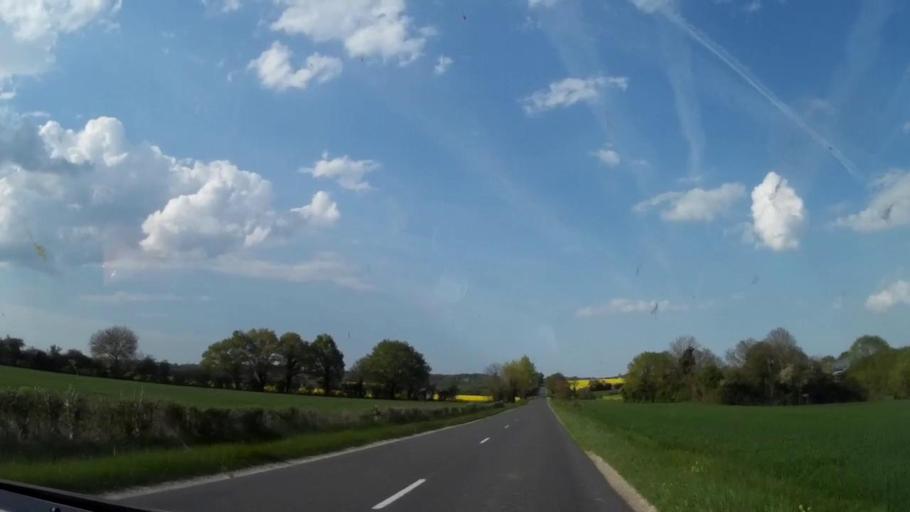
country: FR
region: Centre
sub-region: Departement du Loir-et-Cher
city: Mondoubleau
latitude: 47.9169
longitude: 0.9317
